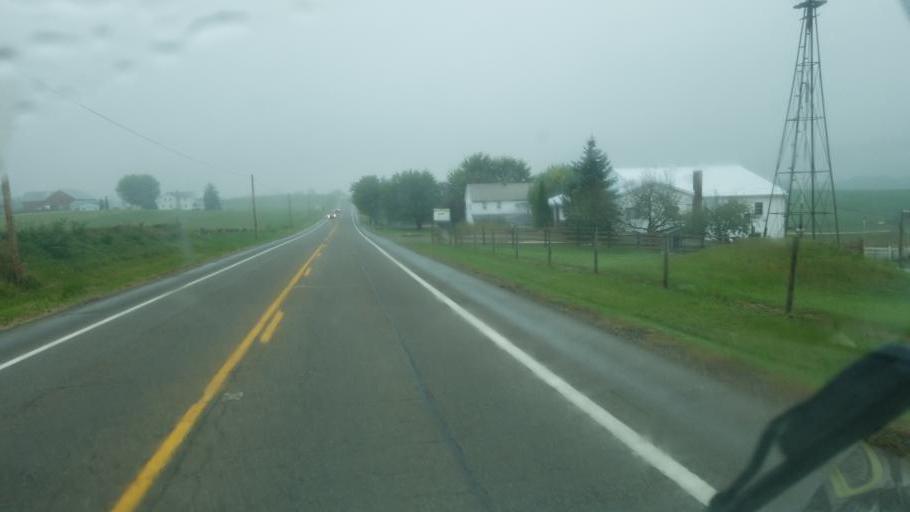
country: US
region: Ohio
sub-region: Tuscarawas County
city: Sugarcreek
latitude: 40.5938
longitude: -81.7538
